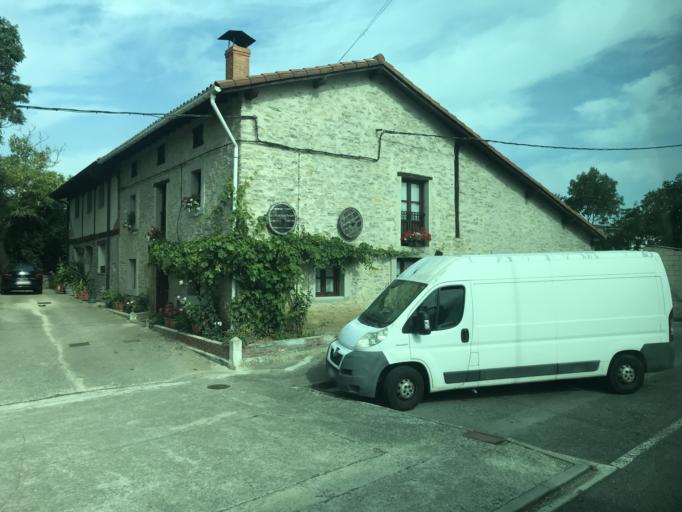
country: ES
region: Basque Country
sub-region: Provincia de Guipuzcoa
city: Leintz-Gatzaga
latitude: 42.9444
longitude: -2.6382
